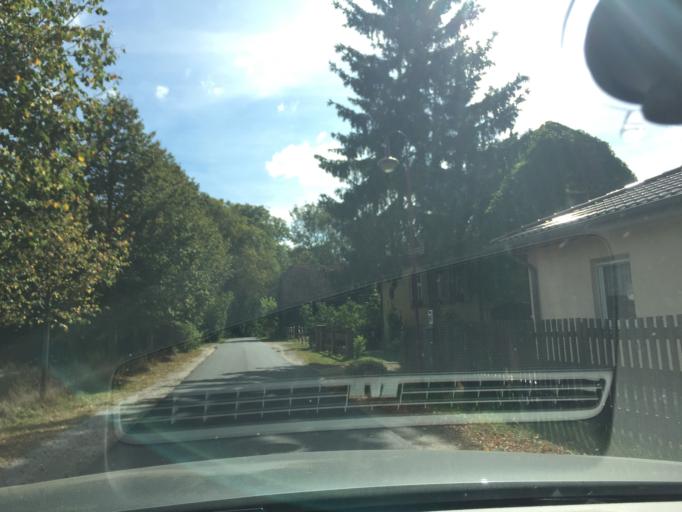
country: DE
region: Brandenburg
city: Spreenhagen
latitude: 52.3870
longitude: 13.8909
